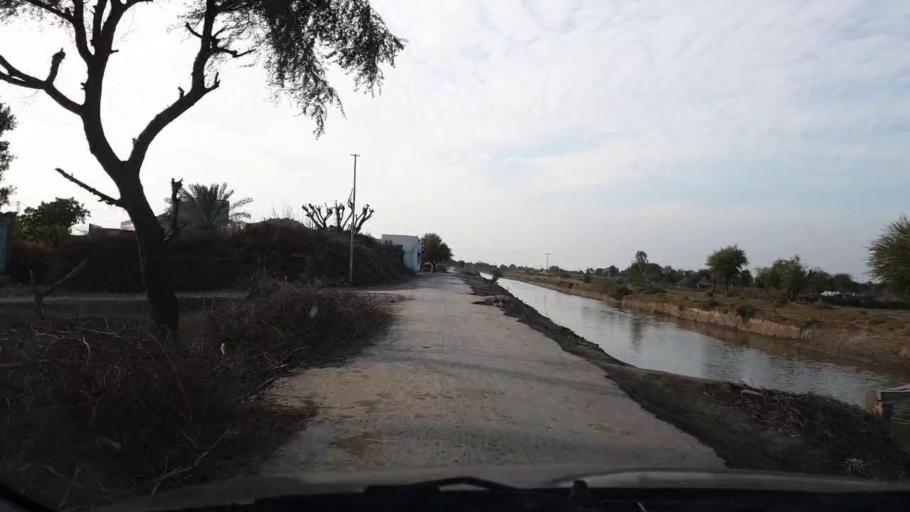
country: PK
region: Sindh
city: Jhol
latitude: 25.9544
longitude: 68.8498
